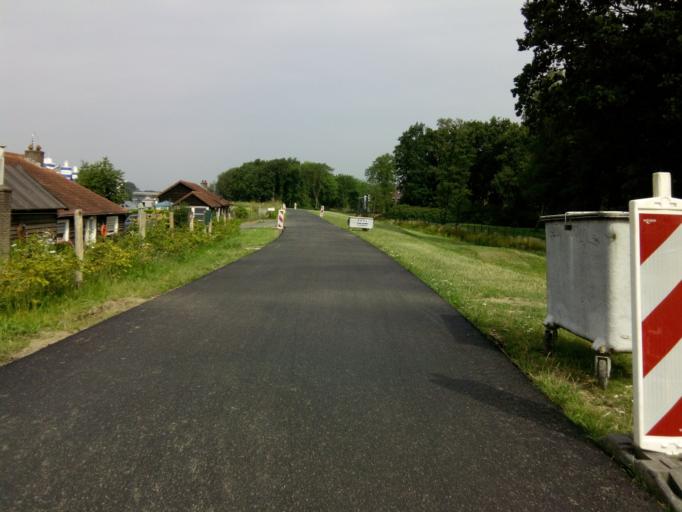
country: NL
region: Utrecht
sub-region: Gemeente Amersfoort
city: Hoogland
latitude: 52.1678
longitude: 5.3718
